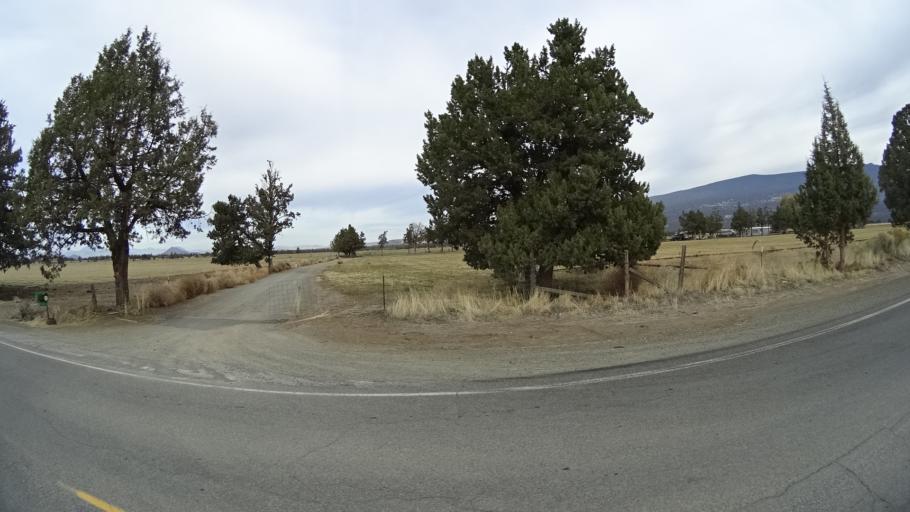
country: US
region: California
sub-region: Siskiyou County
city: Weed
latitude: 41.5962
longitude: -122.3358
